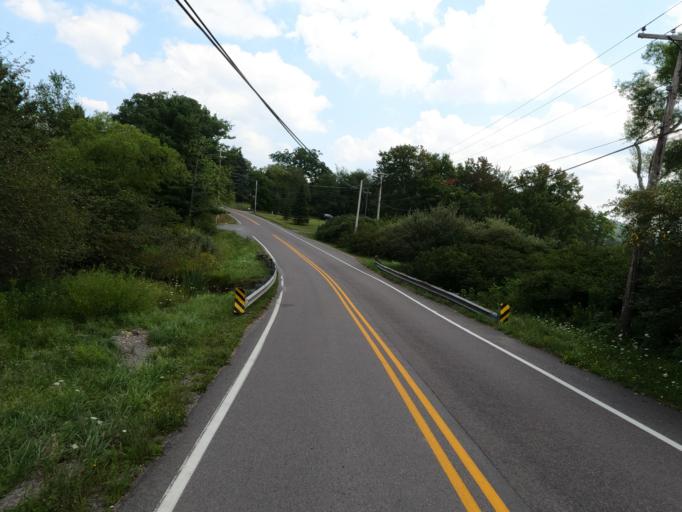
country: US
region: Maryland
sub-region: Garrett County
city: Oakland
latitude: 39.5598
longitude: -79.3581
